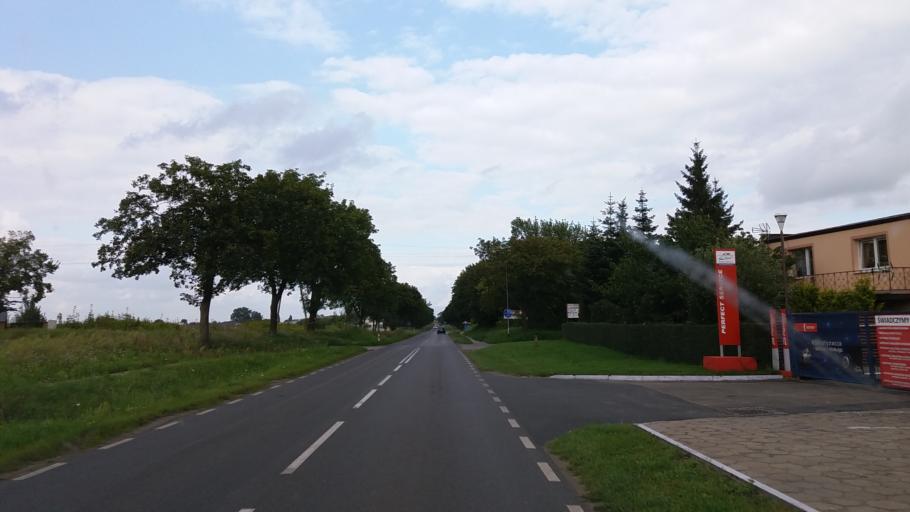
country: PL
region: West Pomeranian Voivodeship
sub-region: Powiat choszczenski
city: Choszczno
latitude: 53.1573
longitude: 15.3910
